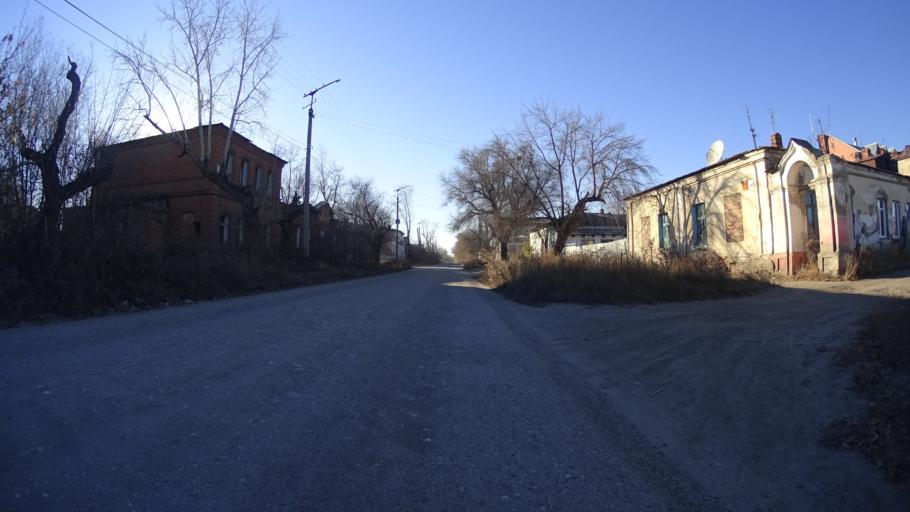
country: RU
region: Chelyabinsk
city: Troitsk
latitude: 54.0801
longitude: 61.5567
